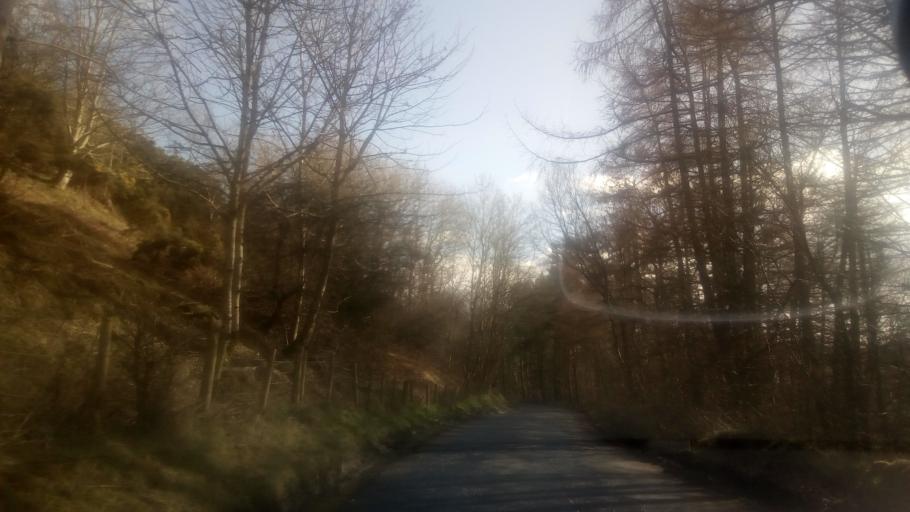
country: GB
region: Scotland
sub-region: The Scottish Borders
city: Hawick
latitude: 55.4155
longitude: -2.8511
